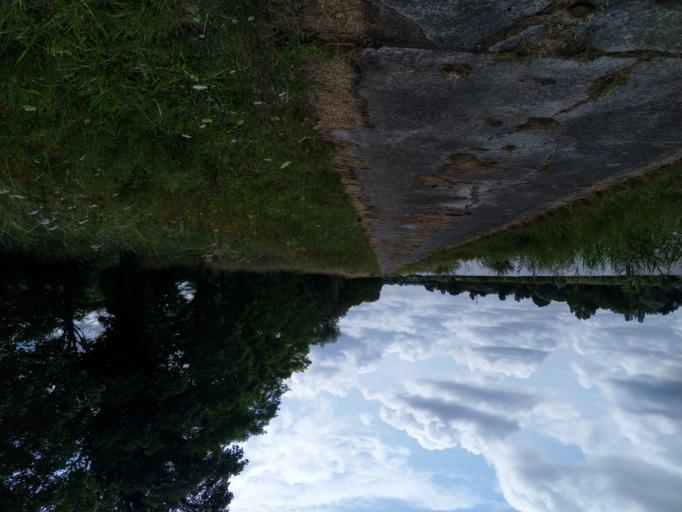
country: BE
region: Wallonia
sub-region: Province du Hainaut
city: Boussu
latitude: 50.4752
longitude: 3.7565
